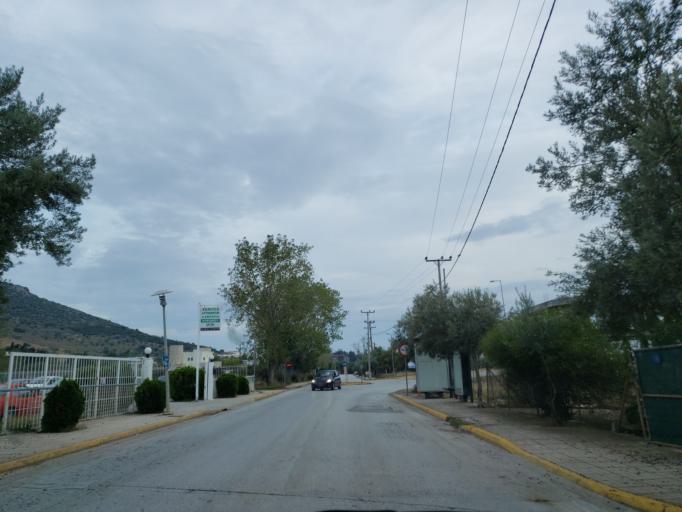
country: GR
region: Attica
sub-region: Nomarchia Anatolikis Attikis
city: Marathonas
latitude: 38.1511
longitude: 23.9638
